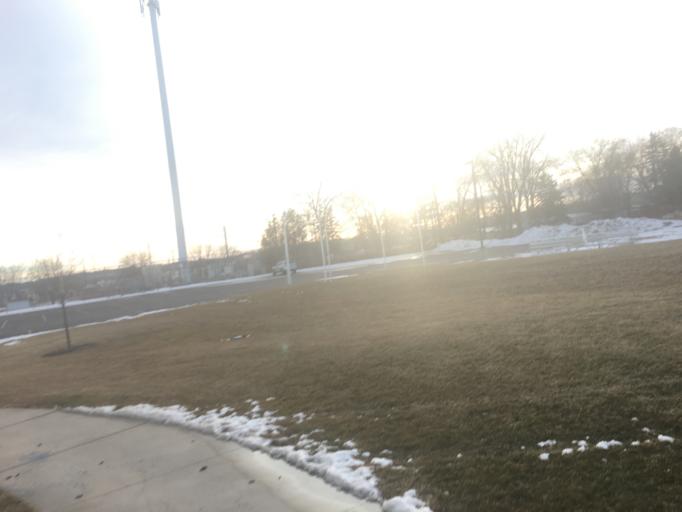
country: US
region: Minnesota
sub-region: Olmsted County
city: Rochester
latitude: 44.0345
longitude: -92.4852
